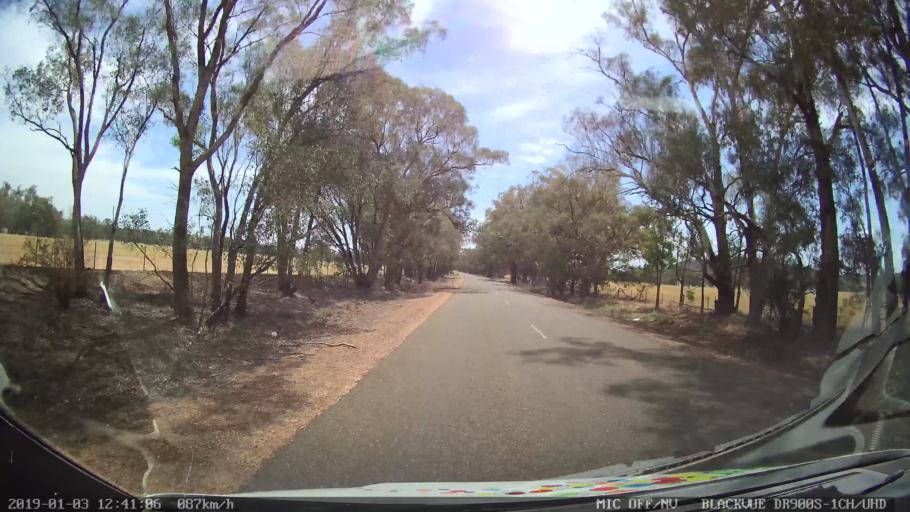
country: AU
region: New South Wales
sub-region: Weddin
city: Grenfell
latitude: -33.8041
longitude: 148.2144
